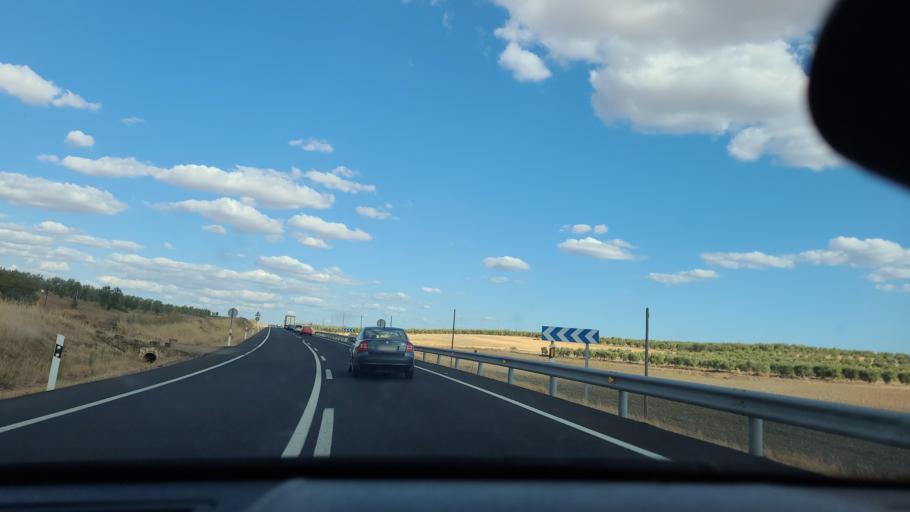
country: ES
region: Extremadura
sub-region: Provincia de Badajoz
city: Berlanga
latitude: 38.2681
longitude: -5.7885
